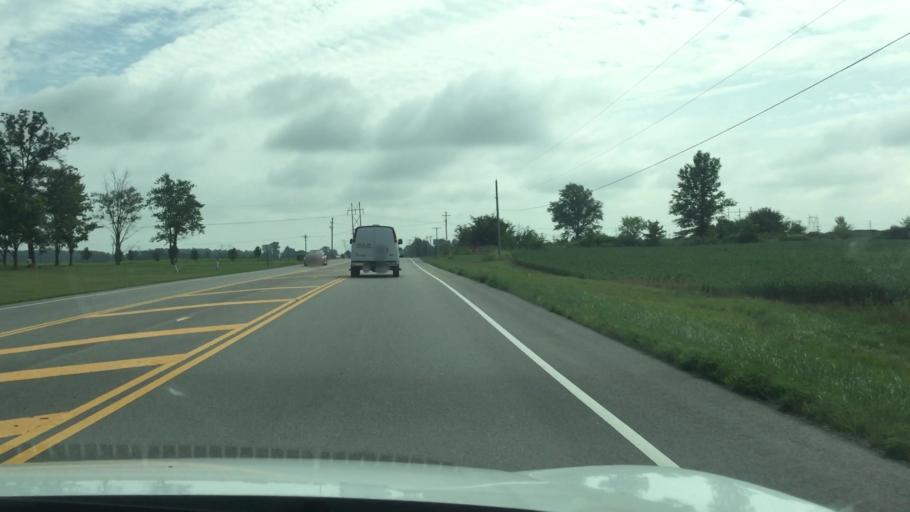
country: US
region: Ohio
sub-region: Union County
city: Marysville
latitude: 40.2056
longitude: -83.4026
